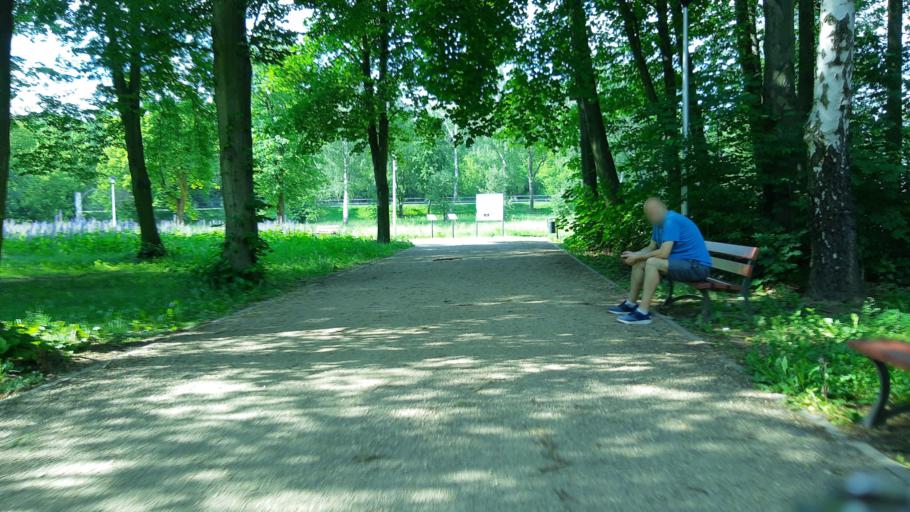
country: PL
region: Lodz Voivodeship
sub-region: Powiat sieradzki
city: Sieradz
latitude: 51.5980
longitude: 18.7534
